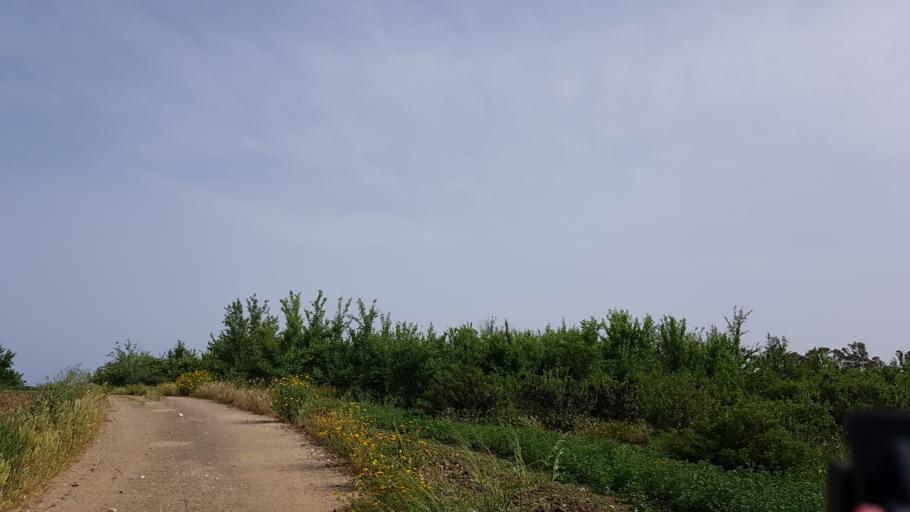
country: IT
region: Apulia
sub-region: Provincia di Brindisi
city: La Rosa
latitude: 40.5910
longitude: 18.0371
